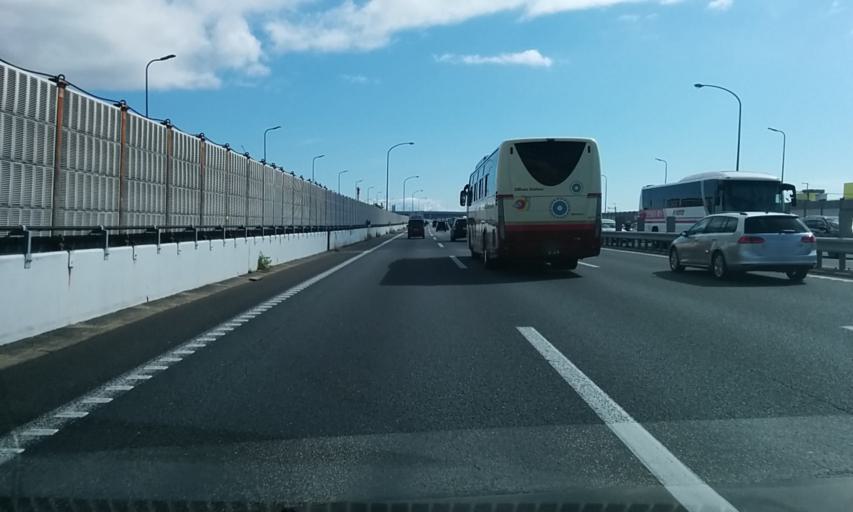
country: JP
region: Hyogo
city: Kawanishi
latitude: 34.8112
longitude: 135.4107
